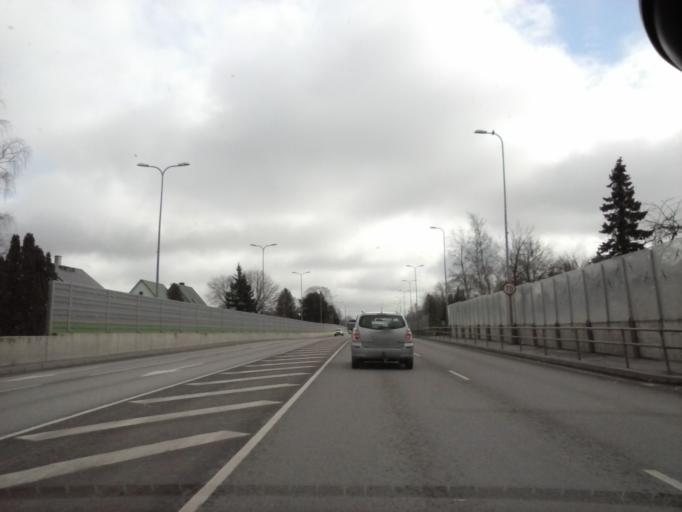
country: EE
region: Harju
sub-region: Tallinna linn
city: Tallinn
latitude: 59.4074
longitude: 24.8071
